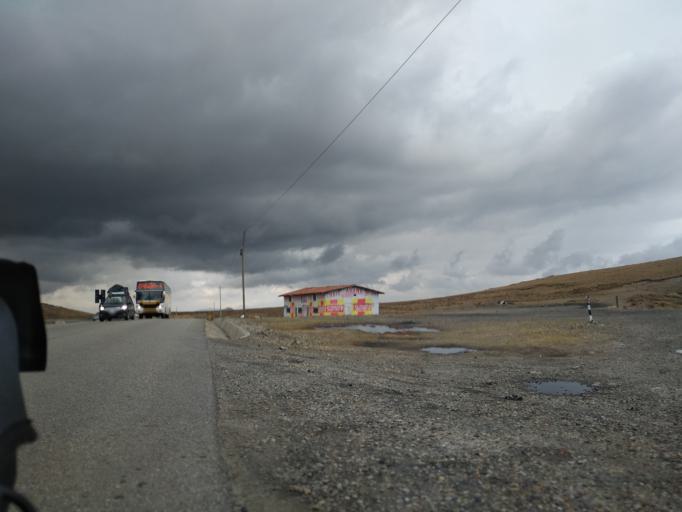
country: PE
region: La Libertad
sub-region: Provincia de Santiago de Chuco
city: Quiruvilca
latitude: -7.9904
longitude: -78.2874
